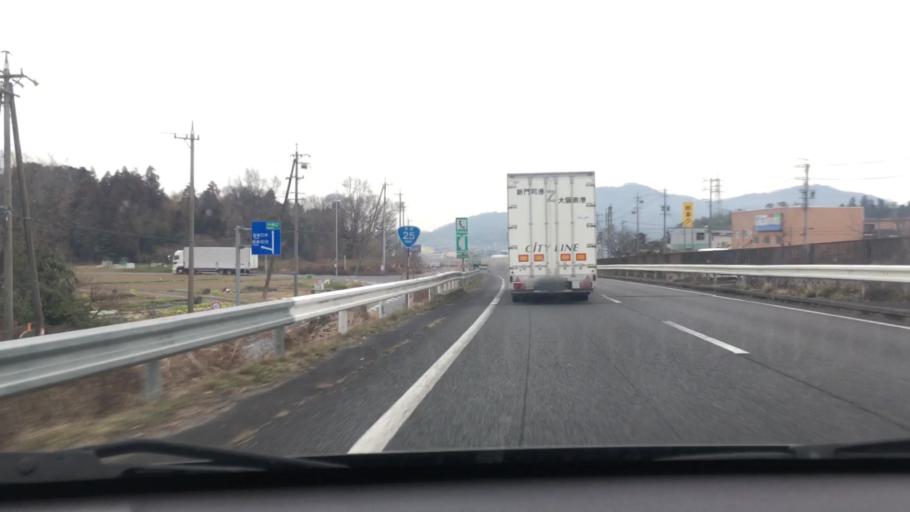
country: JP
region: Mie
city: Ueno-ebisumachi
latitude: 34.7628
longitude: 136.1546
